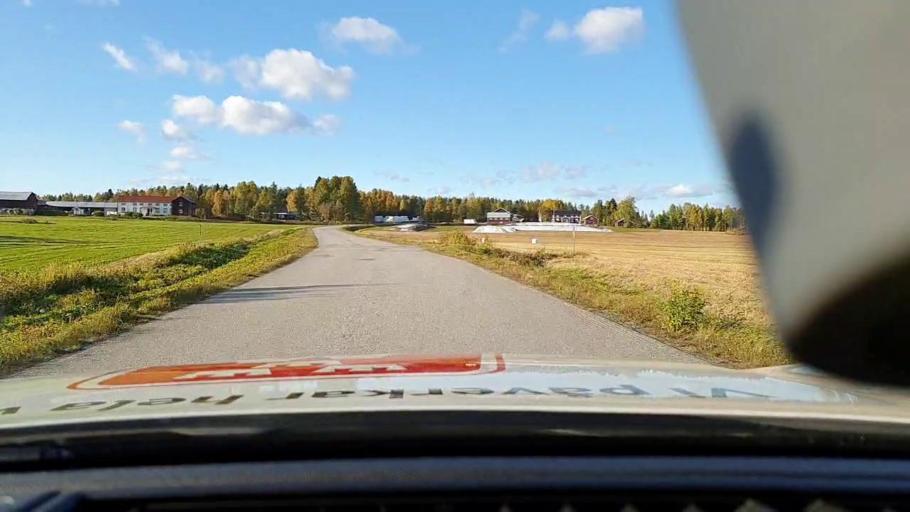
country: SE
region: Norrbotten
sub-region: Pitea Kommun
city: Norrfjarden
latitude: 65.5241
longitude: 21.4912
